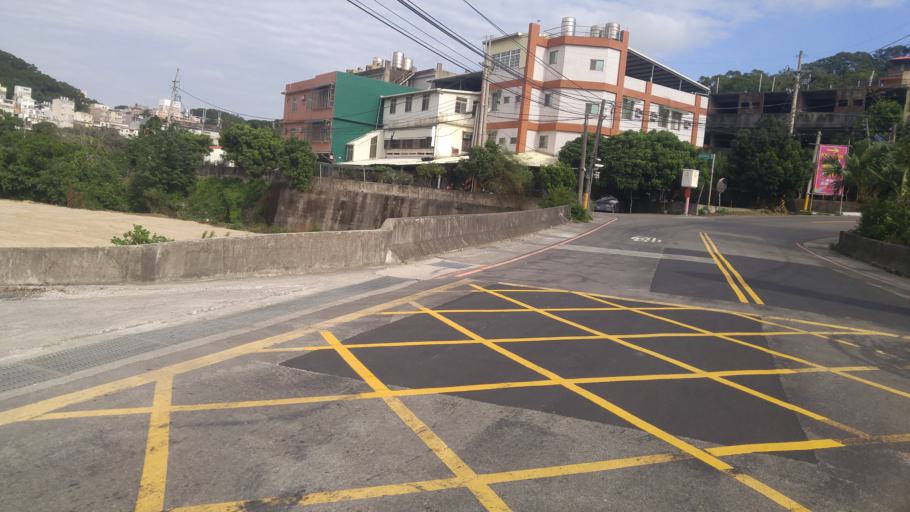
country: TW
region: Taiwan
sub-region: Hsinchu
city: Hsinchu
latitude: 24.7743
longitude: 120.9444
